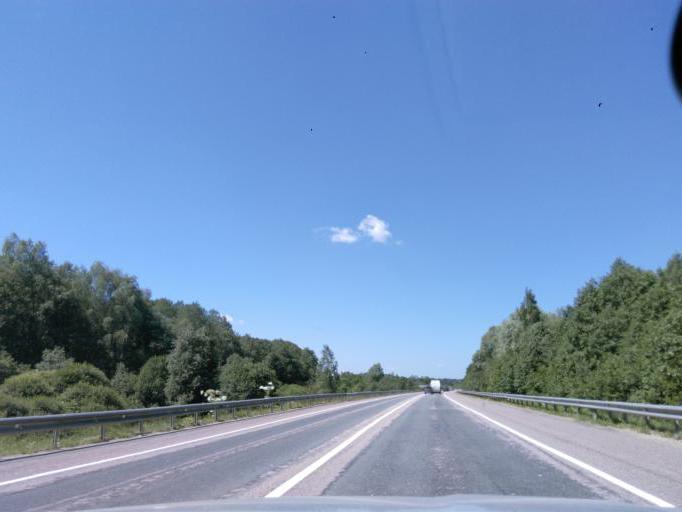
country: RU
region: Moskovskaya
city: Solnechnogorsk
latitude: 56.1450
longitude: 36.9434
